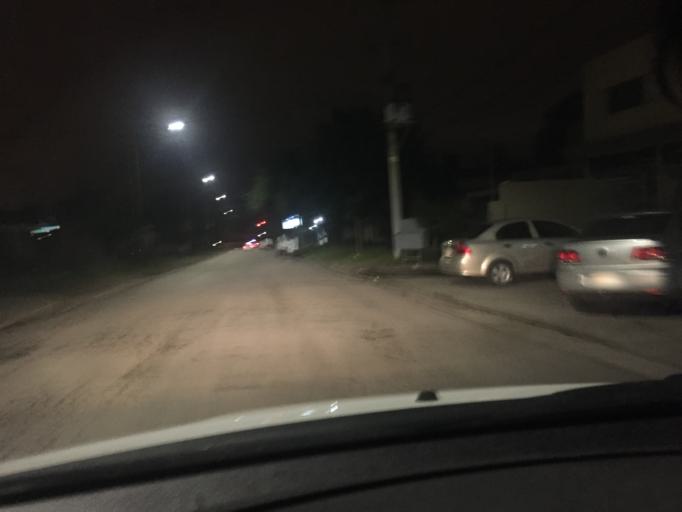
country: AR
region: Cordoba
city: Villa Allende
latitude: -31.3016
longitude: -64.2834
